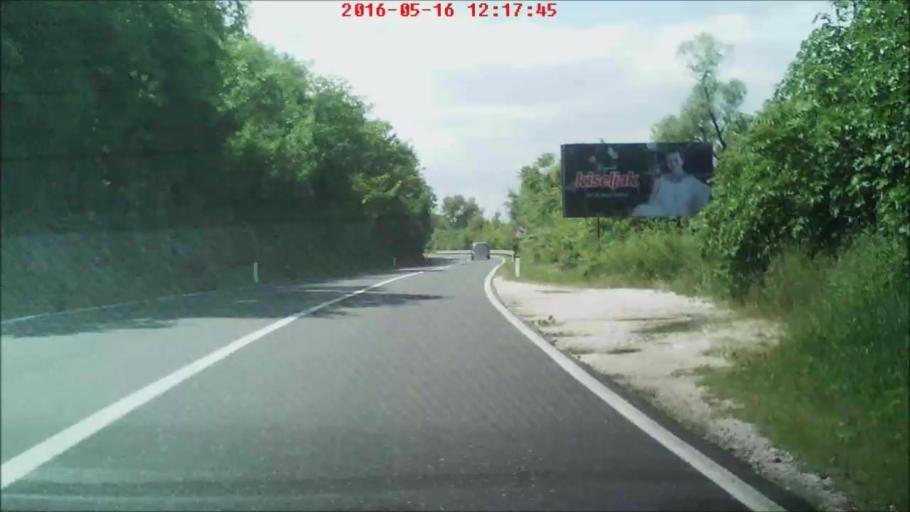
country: HR
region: Dubrovacko-Neretvanska
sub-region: Grad Dubrovnik
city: Metkovic
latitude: 43.0523
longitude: 17.6881
